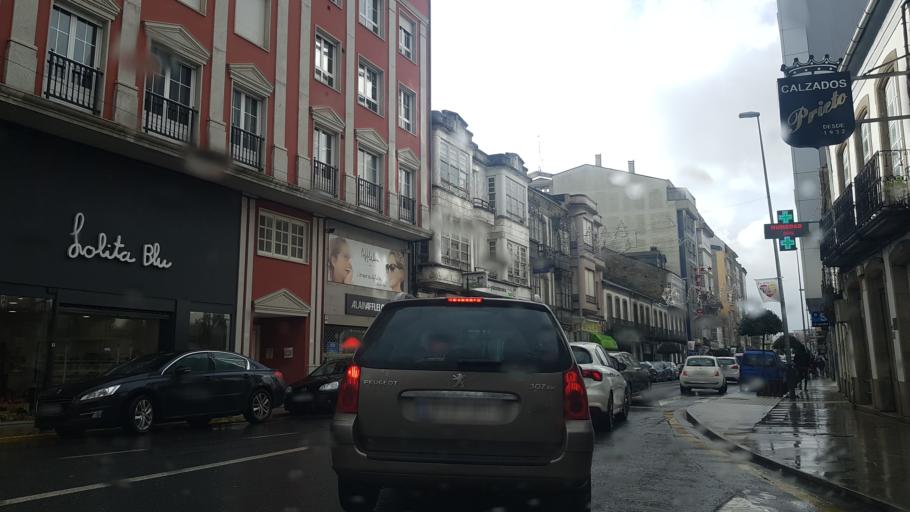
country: ES
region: Galicia
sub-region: Provincia de Lugo
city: Vilalba
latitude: 43.2994
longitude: -7.6789
